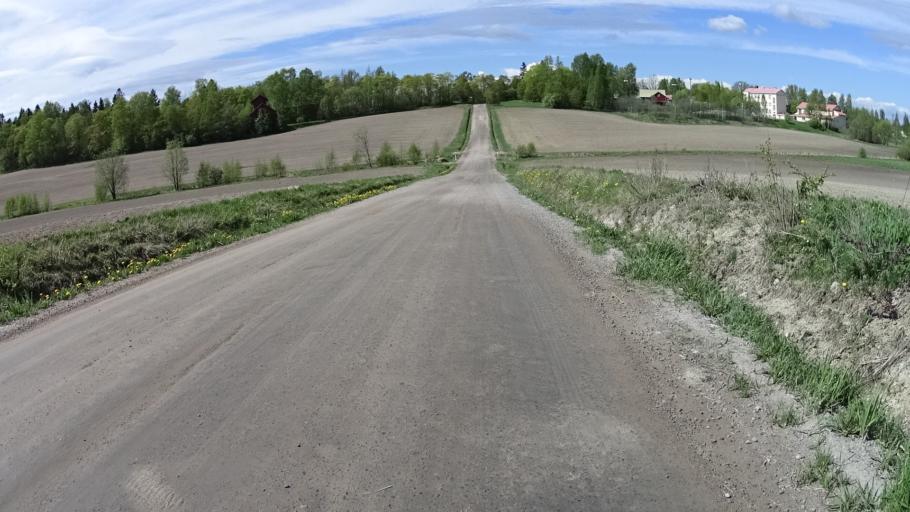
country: FI
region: Uusimaa
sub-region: Helsinki
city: Kilo
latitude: 60.2624
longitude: 24.7866
